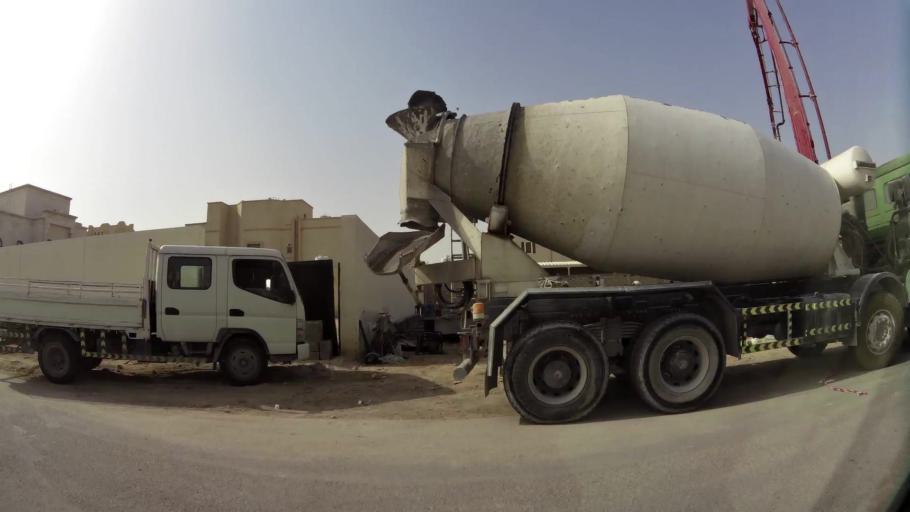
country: QA
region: Baladiyat ar Rayyan
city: Ar Rayyan
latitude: 25.2435
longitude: 51.4463
